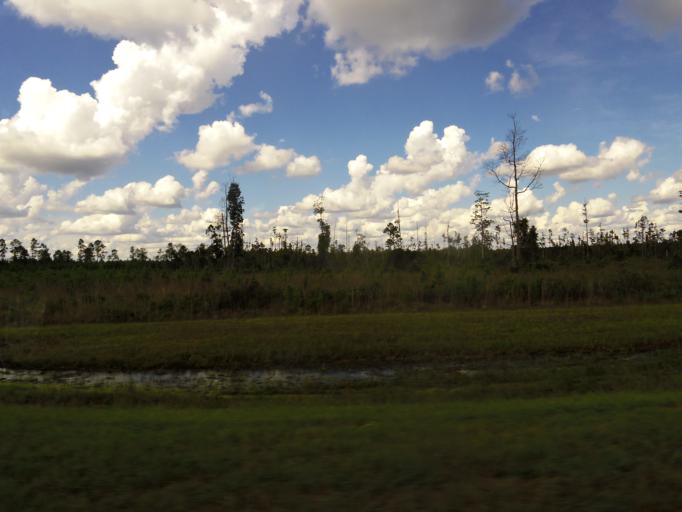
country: US
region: Georgia
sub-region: Echols County
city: Statenville
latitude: 30.7006
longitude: -82.9654
